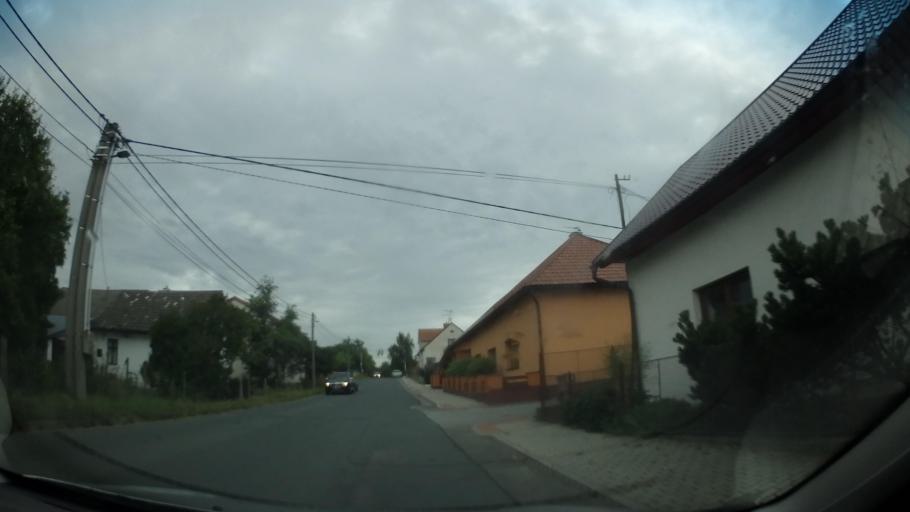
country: CZ
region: Vysocina
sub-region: Okres Zd'ar nad Sazavou
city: Nove Mesto na Morave
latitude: 49.5050
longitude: 16.0350
